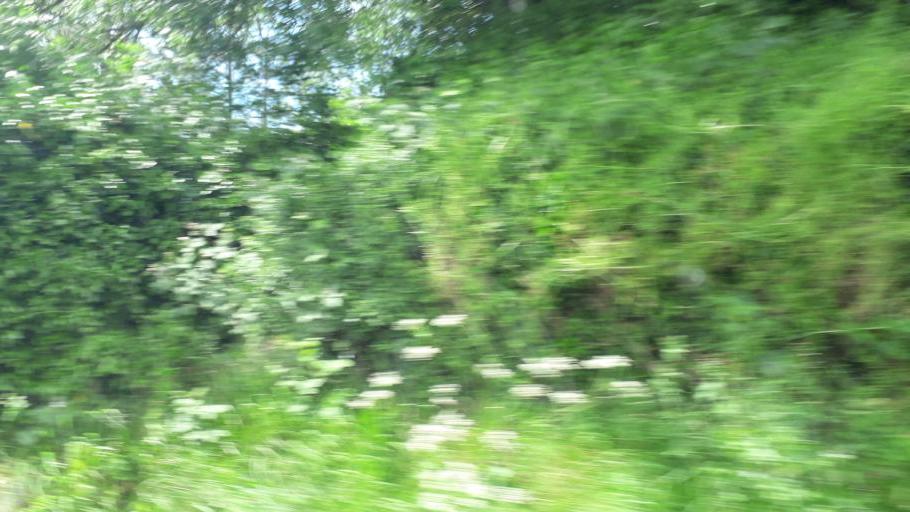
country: IE
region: Leinster
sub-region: Kildare
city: Moone
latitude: 53.0147
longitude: -6.8041
